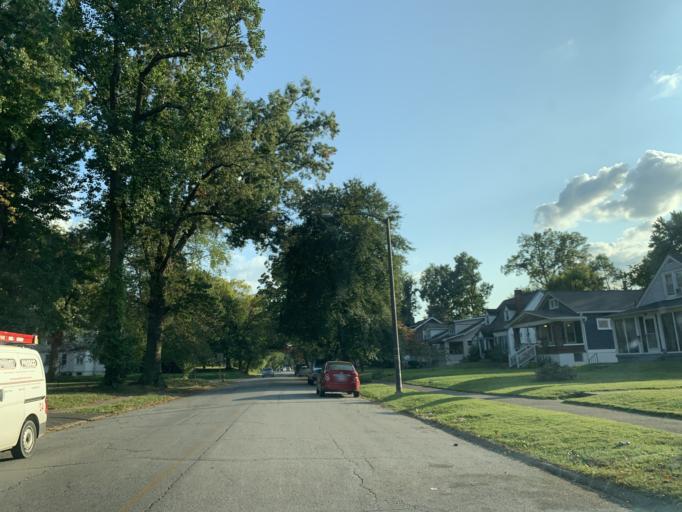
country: US
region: Kentucky
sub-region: Jefferson County
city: Audubon Park
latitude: 38.1858
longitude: -85.7638
